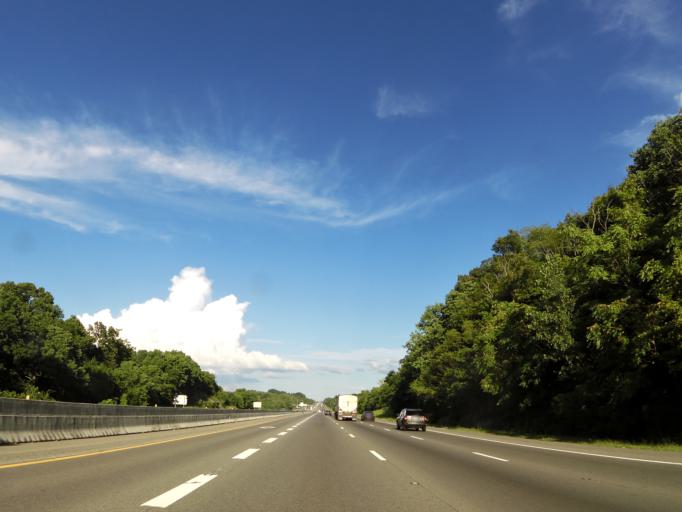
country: US
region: Tennessee
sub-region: Wilson County
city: Green Hill
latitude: 36.1692
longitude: -86.5767
